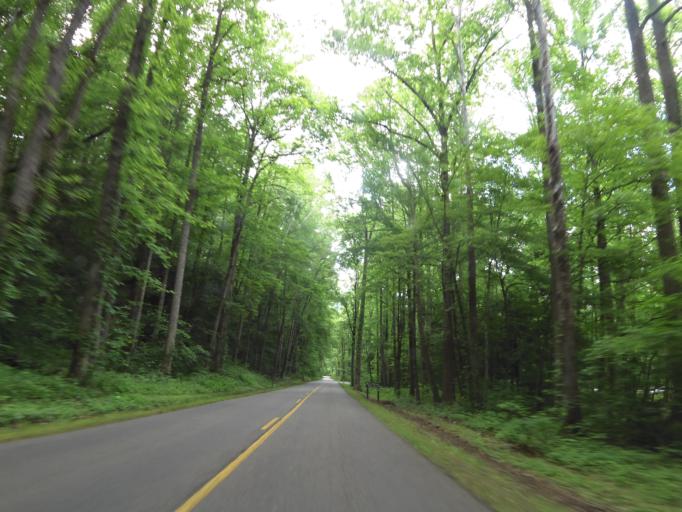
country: US
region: Tennessee
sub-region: Sevier County
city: Gatlinburg
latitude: 35.6772
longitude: -83.6476
